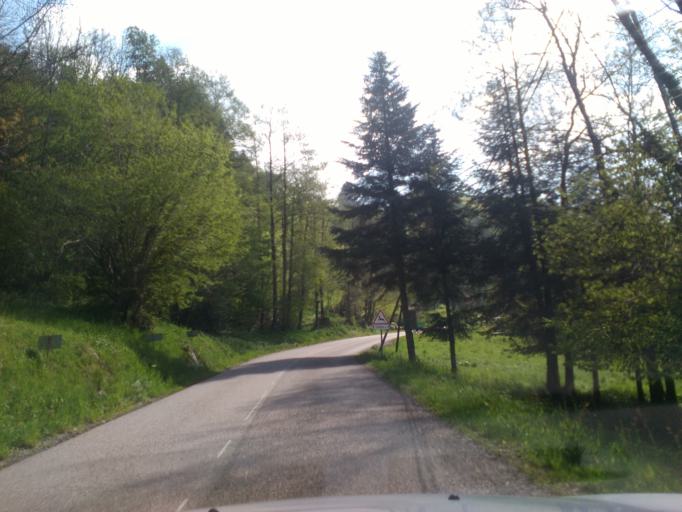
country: FR
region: Lorraine
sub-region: Departement des Vosges
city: Saulxures-sur-Moselotte
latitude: 47.9899
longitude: 6.7705
